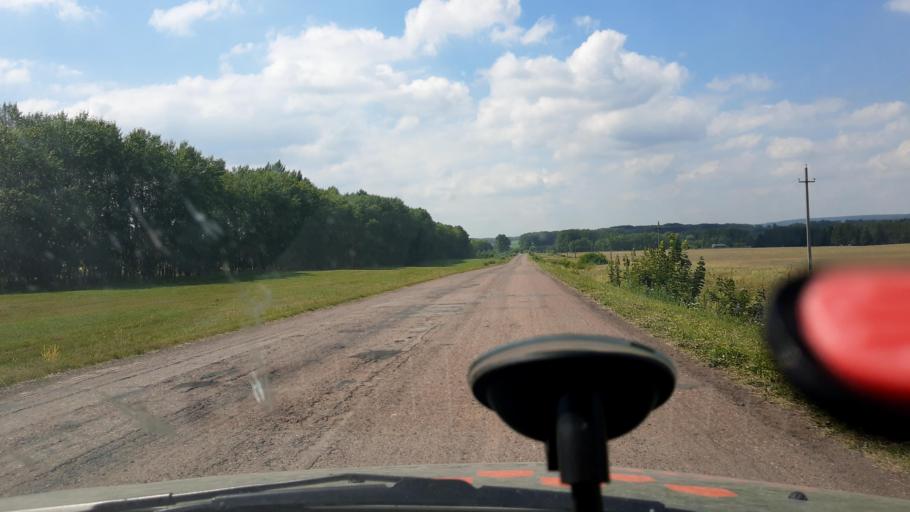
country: RU
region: Bashkortostan
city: Chekmagush
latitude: 54.8860
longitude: 54.5885
